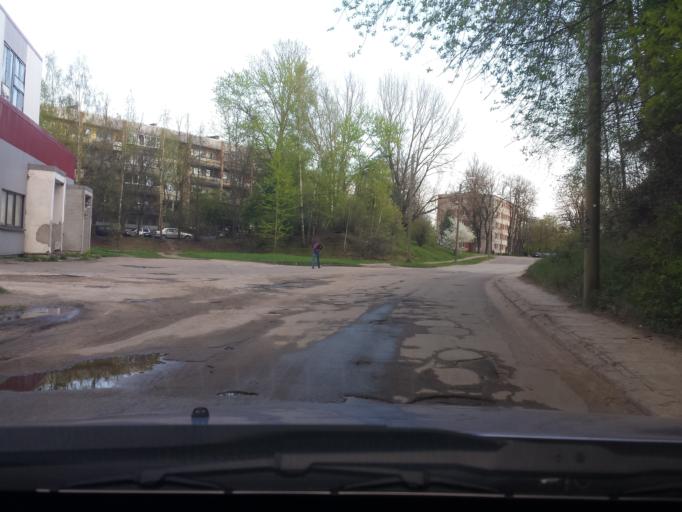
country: LV
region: Riga
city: Jaunciems
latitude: 56.9940
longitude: 24.2274
